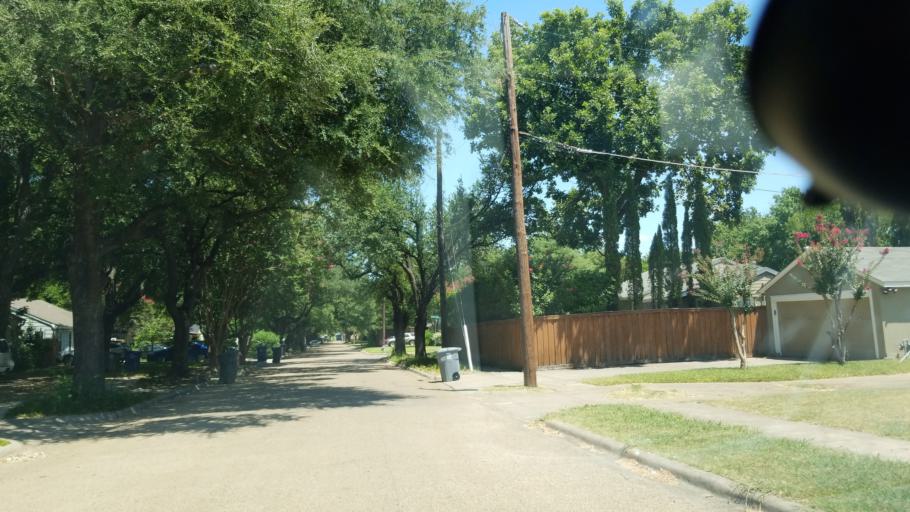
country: US
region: Texas
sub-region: Dallas County
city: Cockrell Hill
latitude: 32.7195
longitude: -96.8436
